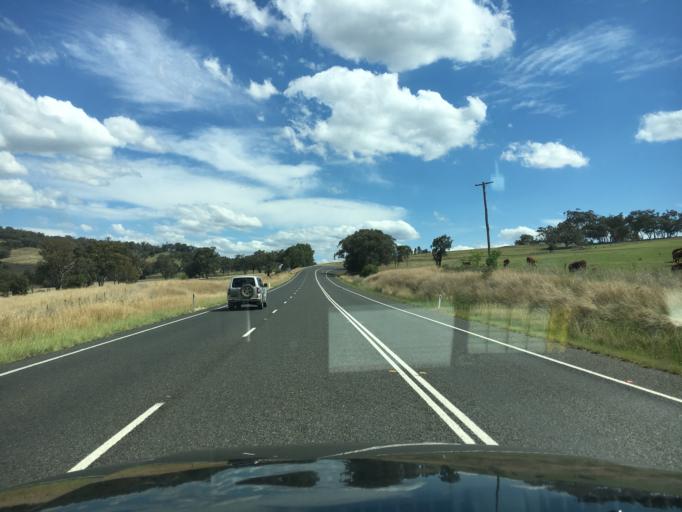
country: AU
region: New South Wales
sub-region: Liverpool Plains
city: Quirindi
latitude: -31.4370
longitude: 150.8815
